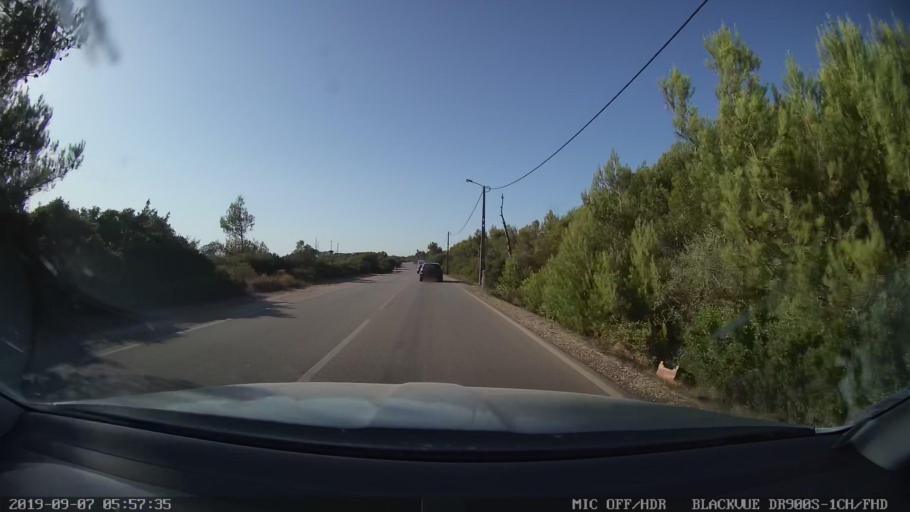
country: PT
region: Setubal
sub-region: Sesimbra
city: Sesimbra
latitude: 38.4524
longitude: -9.0901
